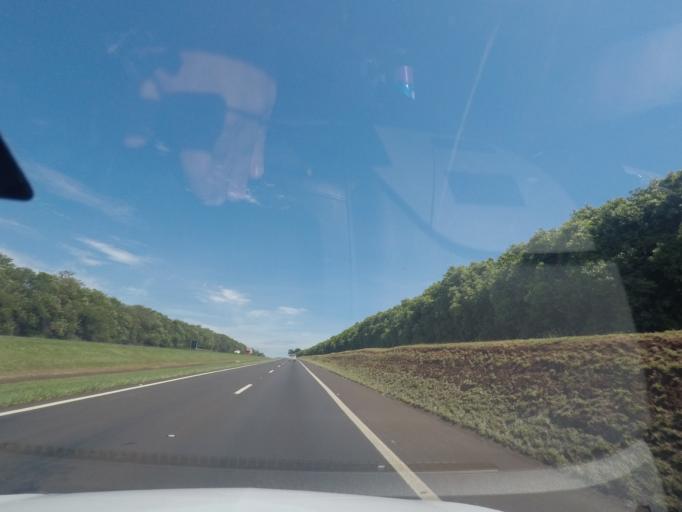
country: BR
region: Sao Paulo
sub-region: Araraquara
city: Araraquara
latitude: -21.8464
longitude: -48.1391
